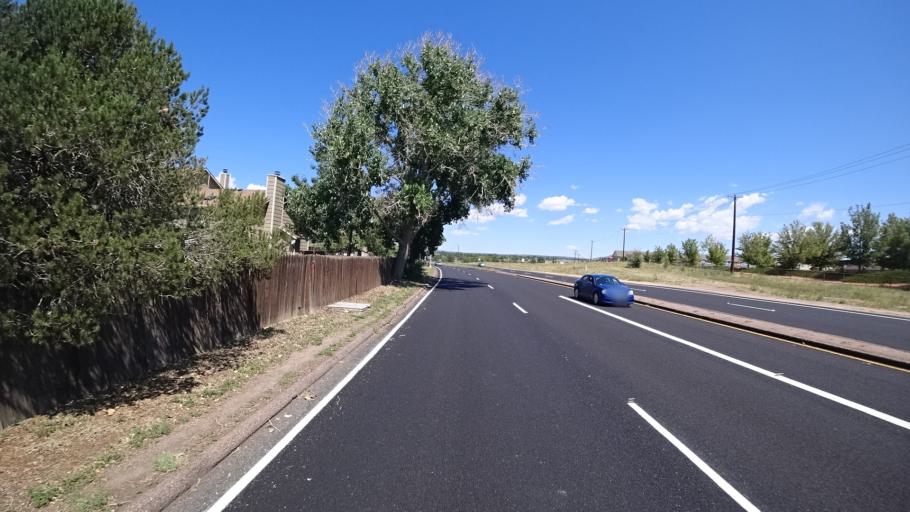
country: US
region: Colorado
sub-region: El Paso County
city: Stratmoor
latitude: 38.7846
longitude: -104.7391
